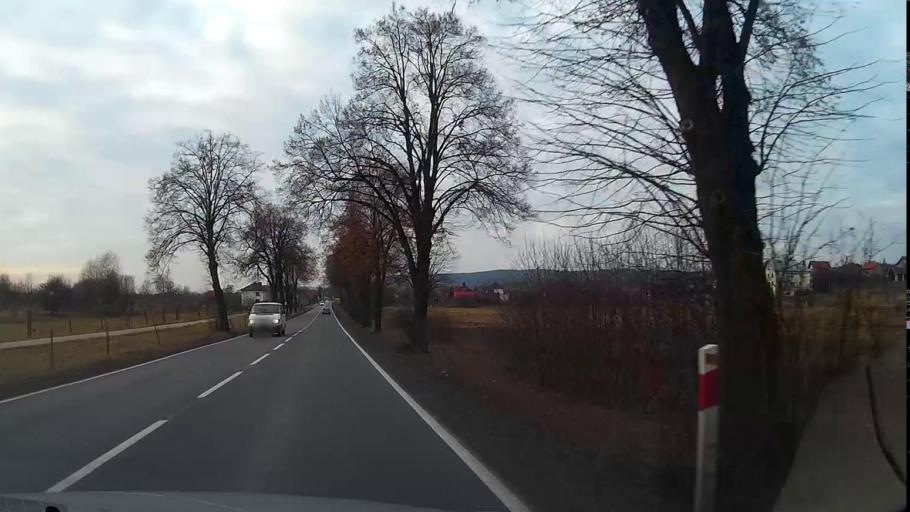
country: PL
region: Lesser Poland Voivodeship
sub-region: Powiat chrzanowski
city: Kwaczala
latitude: 50.0626
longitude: 19.4979
